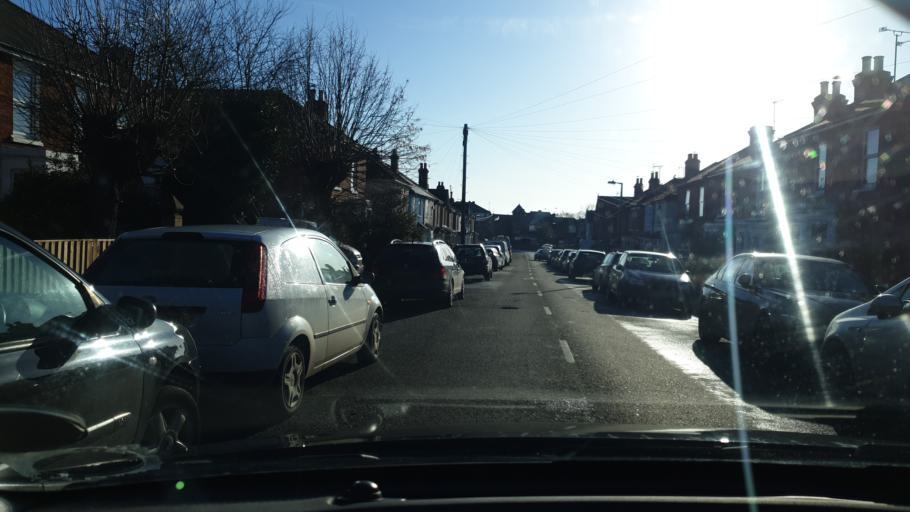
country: GB
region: England
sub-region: Essex
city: Brightlingsea
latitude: 51.8129
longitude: 1.0231
